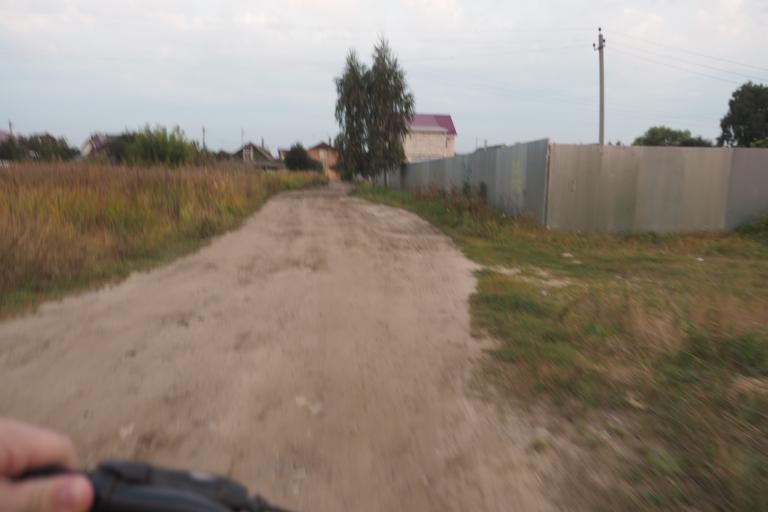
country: RU
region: Moskovskaya
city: Ramenskoye
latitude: 55.5850
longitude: 38.2578
